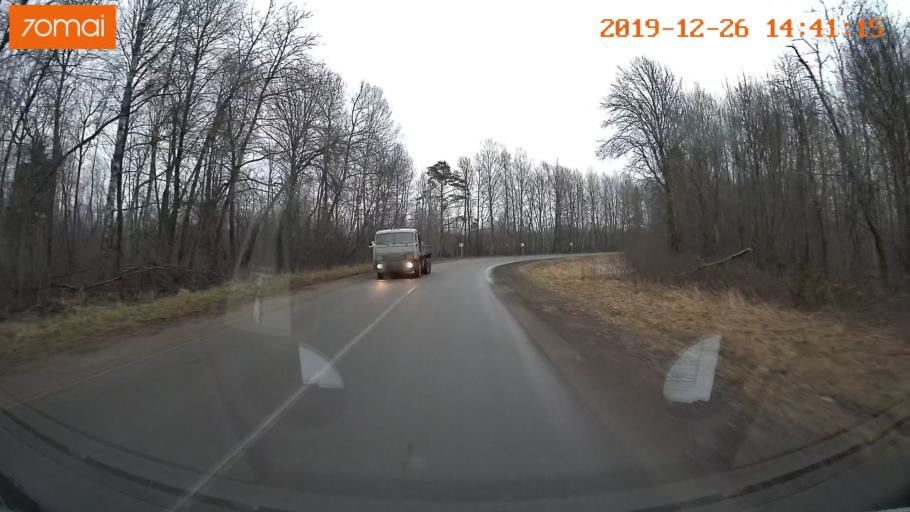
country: RU
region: Jaroslavl
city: Poshekhon'ye
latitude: 58.3725
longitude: 39.0159
